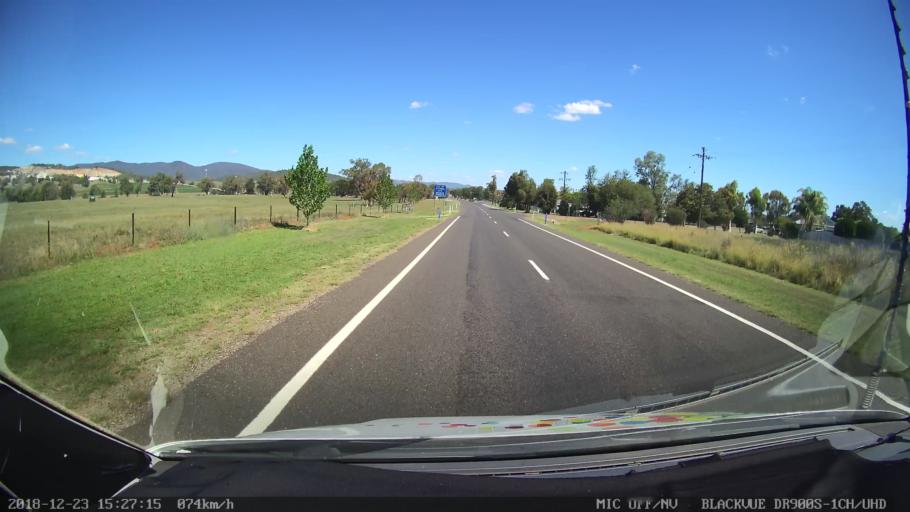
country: AU
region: New South Wales
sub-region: Tamworth Municipality
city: East Tamworth
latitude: -30.9258
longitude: 150.8442
